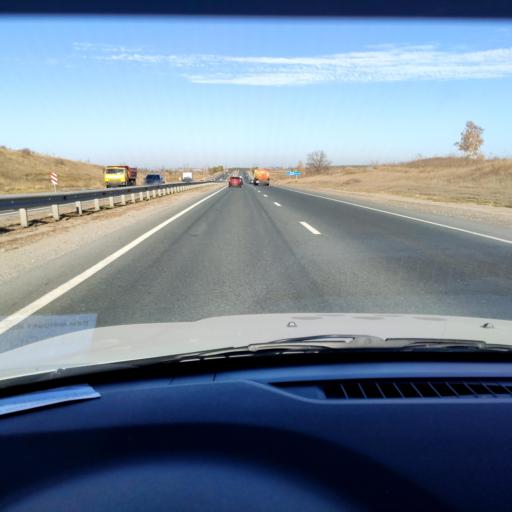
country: RU
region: Samara
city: Zhigulevsk
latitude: 53.5073
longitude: 49.5383
